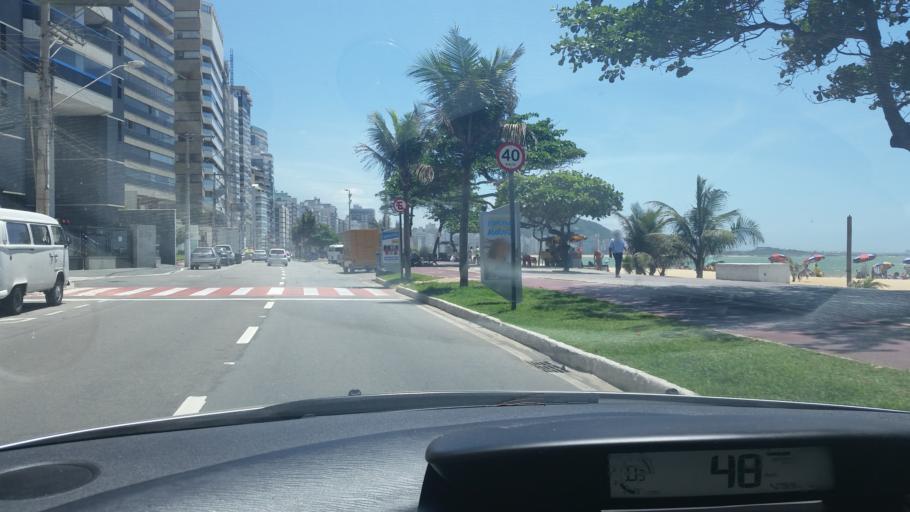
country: BR
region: Espirito Santo
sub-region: Vila Velha
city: Vila Velha
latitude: -20.3508
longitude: -40.2838
